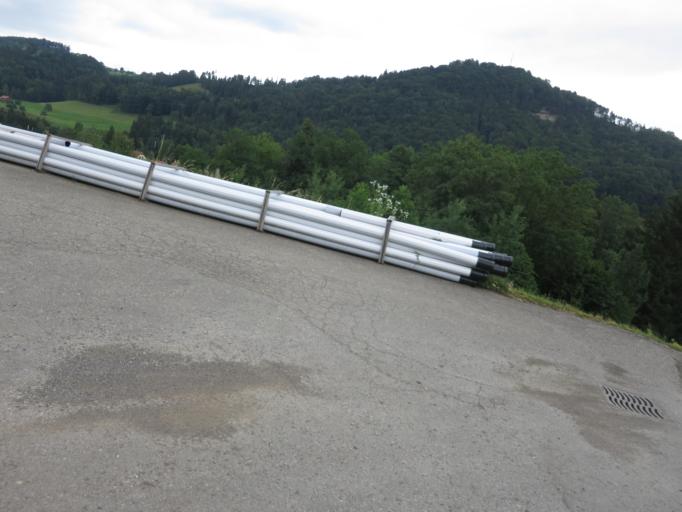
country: CH
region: Saint Gallen
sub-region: Wahlkreis Toggenburg
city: Buetschwil
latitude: 47.3552
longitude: 9.0780
